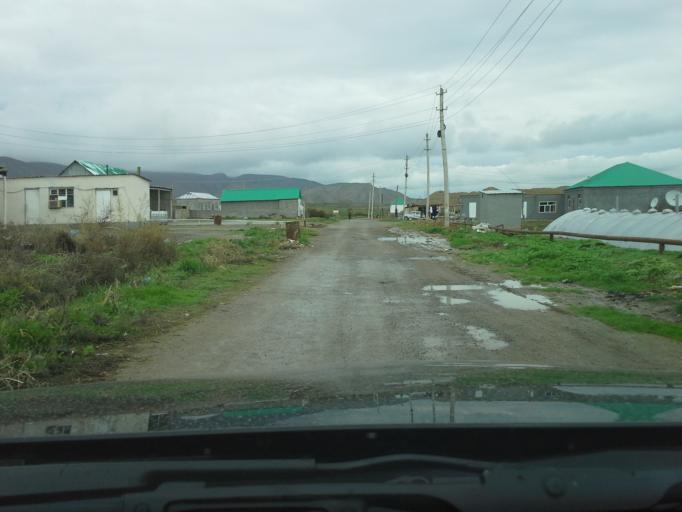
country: TM
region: Ahal
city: Abadan
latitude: 37.9607
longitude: 58.2016
